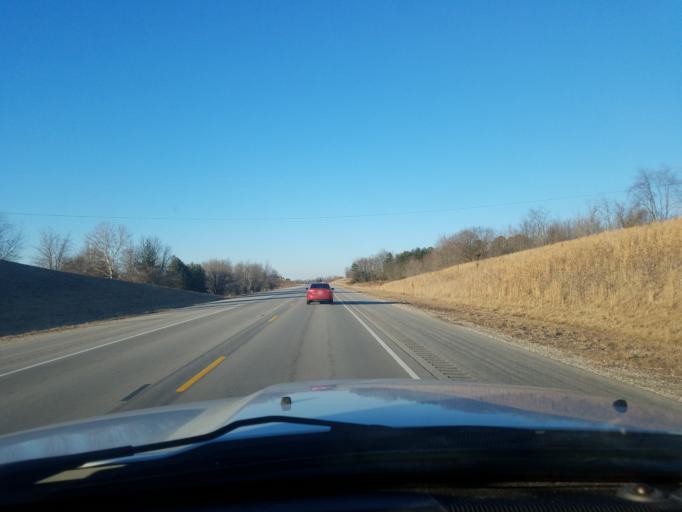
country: US
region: Indiana
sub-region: Perry County
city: Tell City
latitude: 38.1185
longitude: -86.6077
